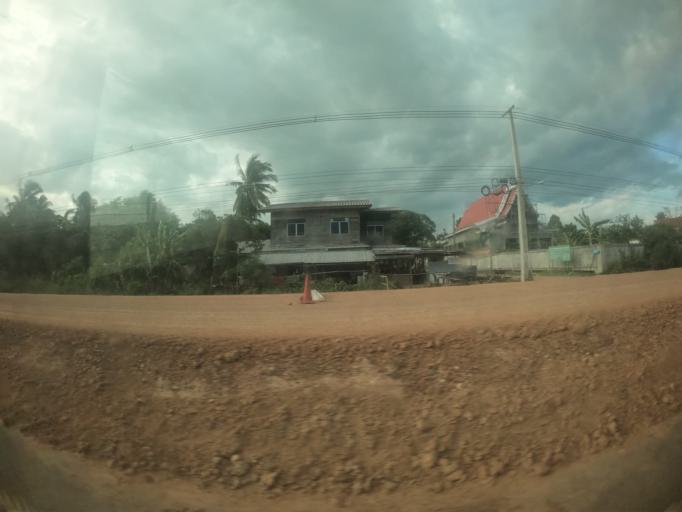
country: TH
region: Surin
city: Kap Choeng
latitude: 14.4633
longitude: 103.6480
